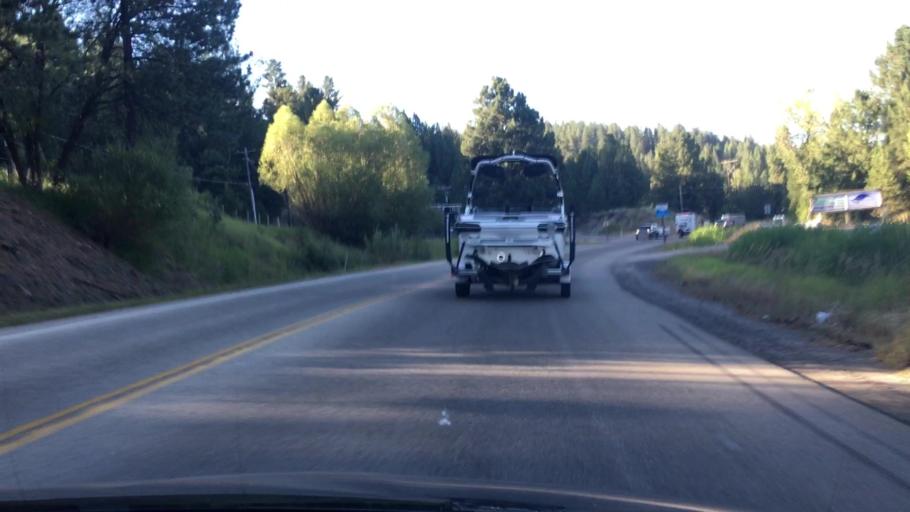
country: US
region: Idaho
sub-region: Valley County
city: Cascade
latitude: 44.5216
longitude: -116.0462
